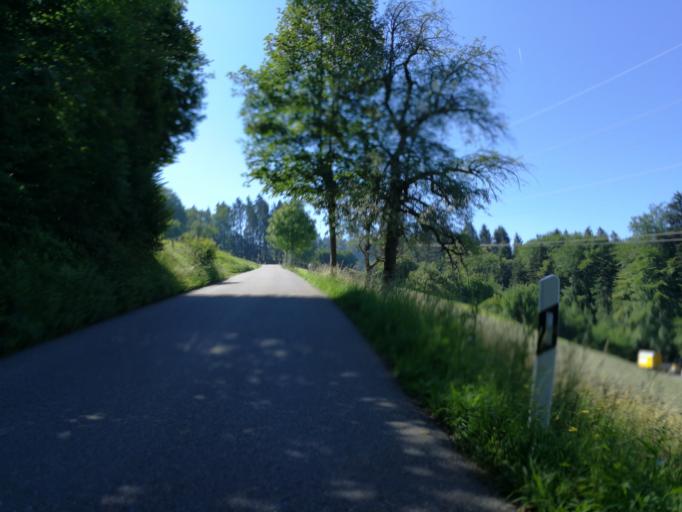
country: CH
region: Zurich
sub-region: Bezirk Hinwil
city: Hadlikon
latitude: 47.2957
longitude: 8.8748
